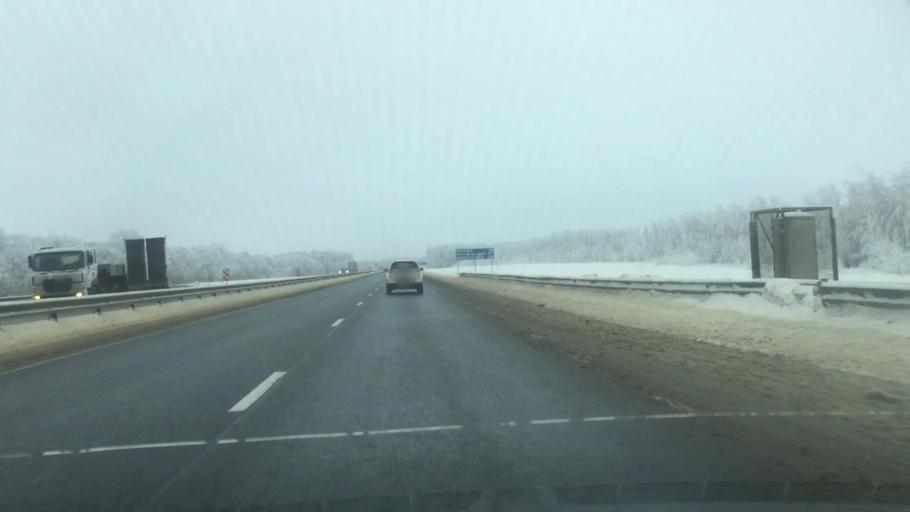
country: RU
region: Lipetsk
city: Zadonsk
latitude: 52.4995
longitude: 38.7553
